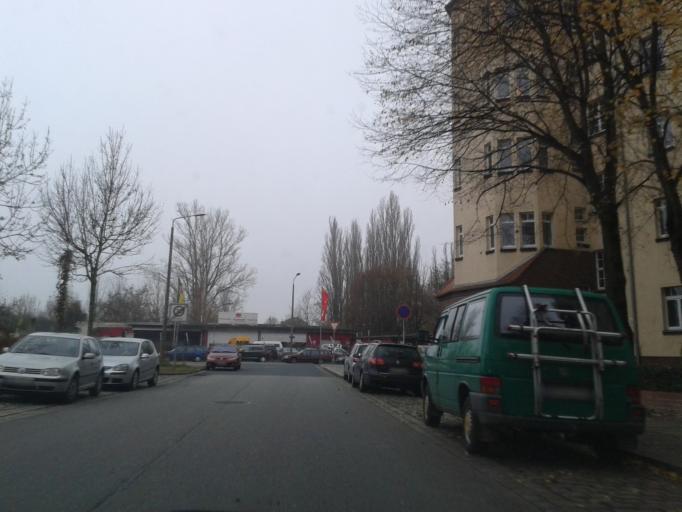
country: DE
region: Saxony
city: Dresden
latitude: 51.0718
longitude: 13.7312
